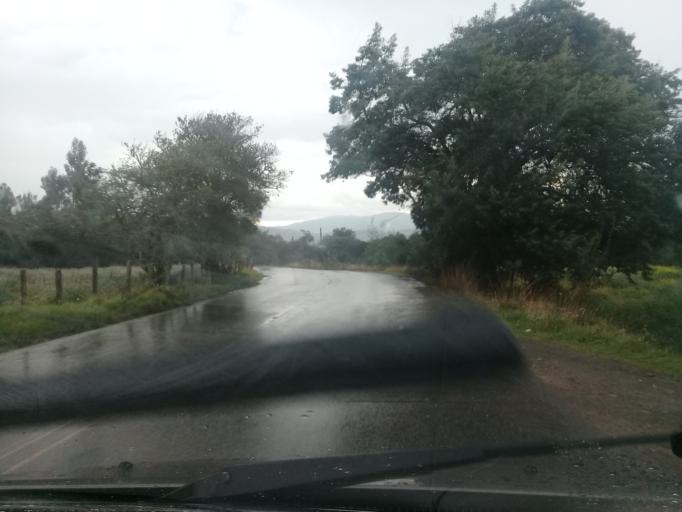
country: CO
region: Cundinamarca
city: Guasca
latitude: 4.8527
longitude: -73.8488
